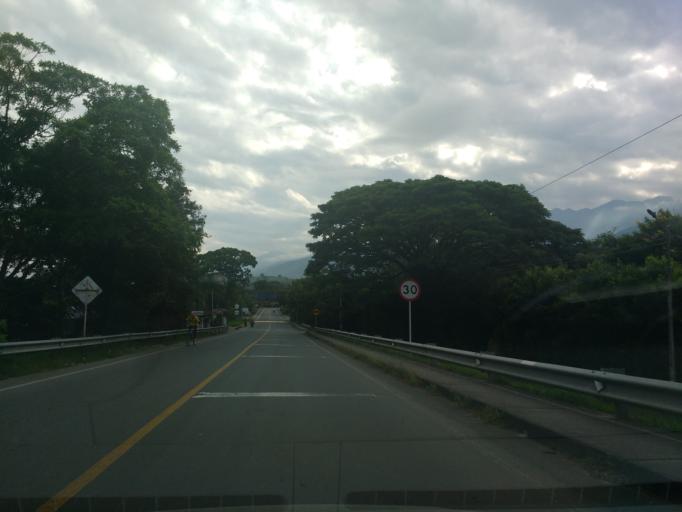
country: CO
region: Cauca
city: Miranda
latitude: 3.2732
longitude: -76.2230
